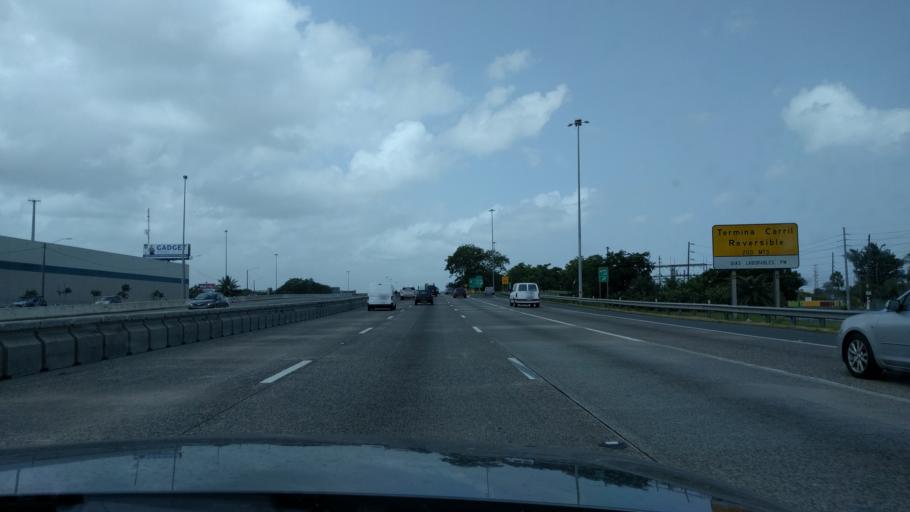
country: PR
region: Catano
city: Catano
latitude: 18.4229
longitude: -66.1382
